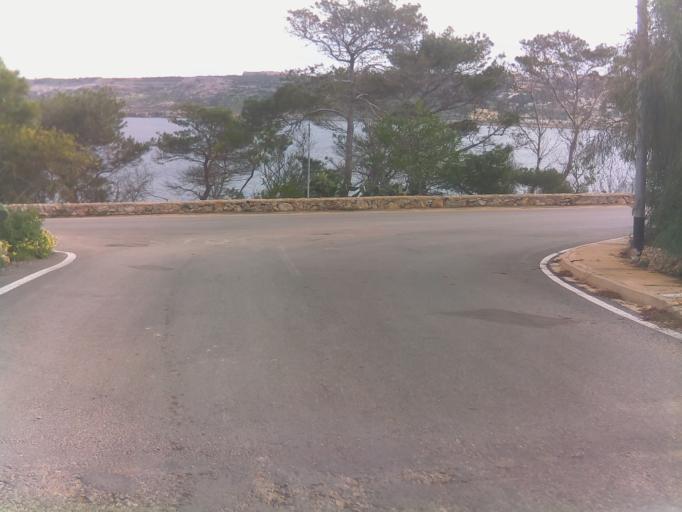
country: MT
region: Il-Mellieha
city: Mellieha
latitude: 35.9861
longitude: 14.3671
